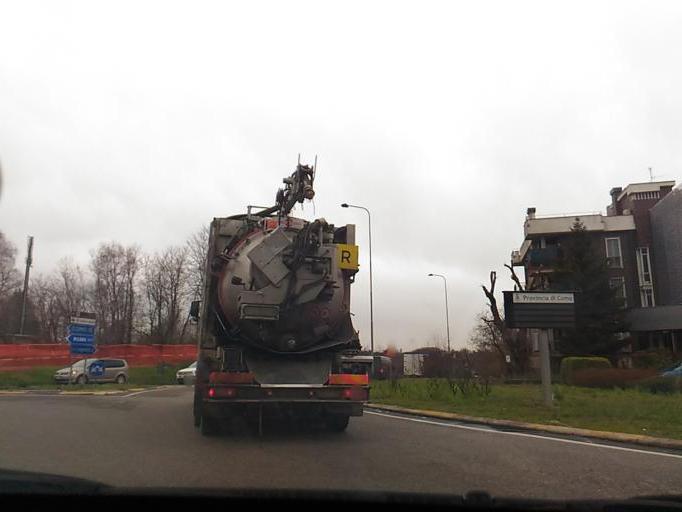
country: IT
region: Lombardy
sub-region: Provincia di Como
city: Novedrate
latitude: 45.6900
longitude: 9.1067
